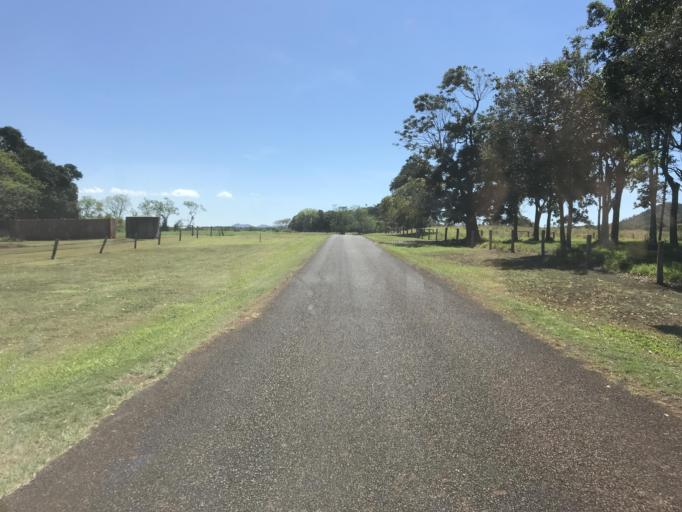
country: AU
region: Queensland
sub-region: Tablelands
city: Atherton
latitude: -17.2773
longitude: 145.5444
